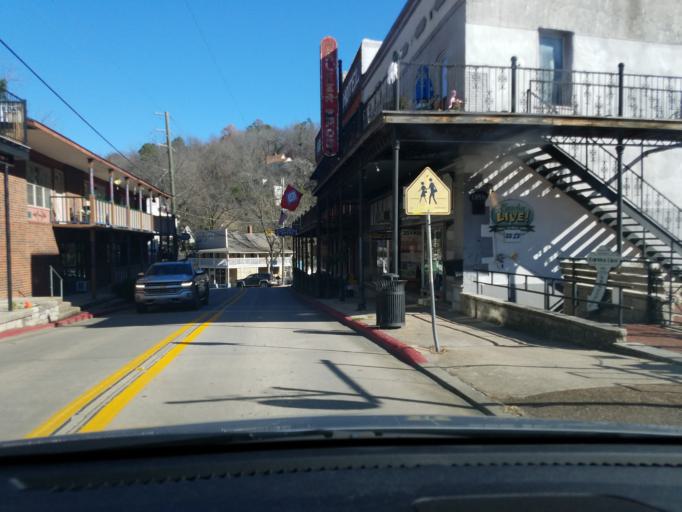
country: US
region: Arkansas
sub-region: Carroll County
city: Eureka Springs
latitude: 36.4023
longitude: -93.7365
